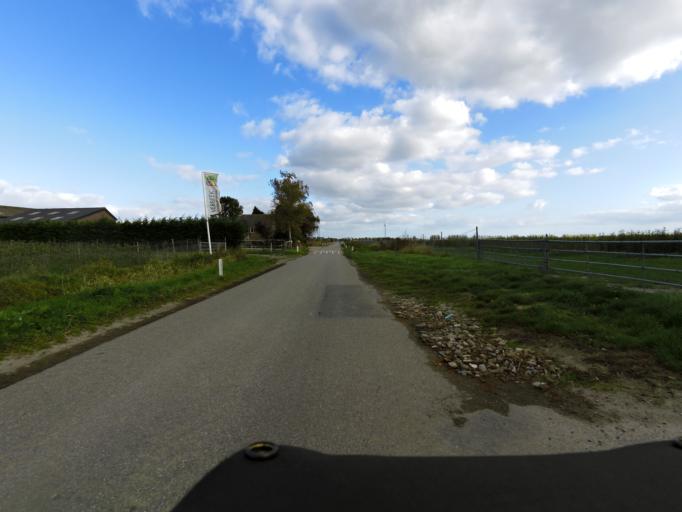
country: NL
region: North Brabant
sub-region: Gemeente Bergen op Zoom
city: Lepelstraat
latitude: 51.5729
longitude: 4.2700
